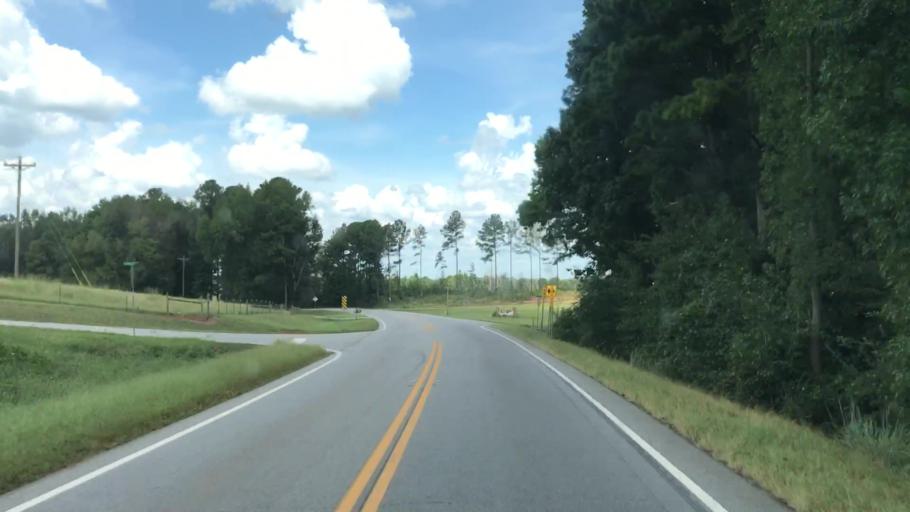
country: US
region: Georgia
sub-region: Greene County
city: Greensboro
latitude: 33.6038
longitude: -83.1981
